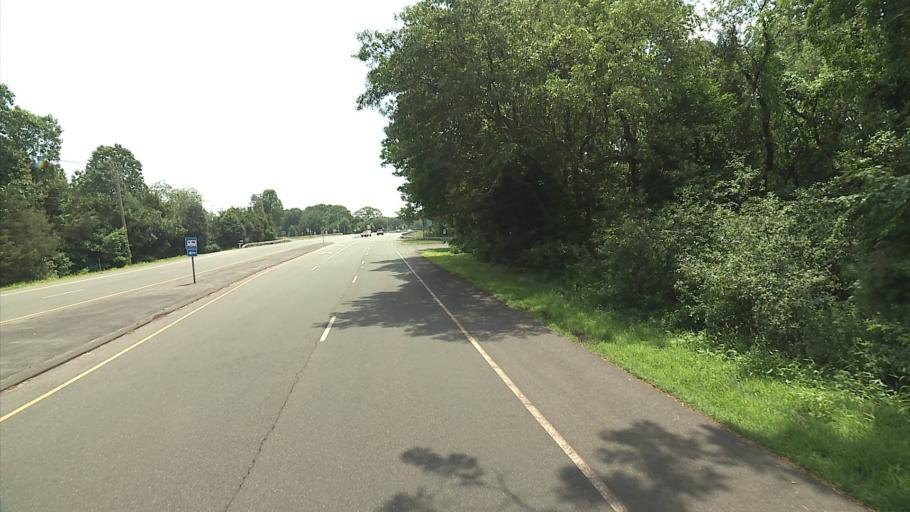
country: US
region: Connecticut
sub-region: New Haven County
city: Madison
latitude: 41.2926
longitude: -72.5724
